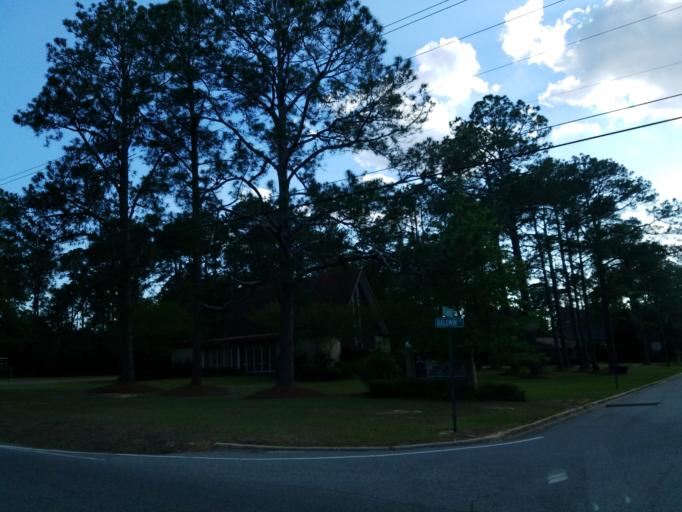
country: US
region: Georgia
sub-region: Tift County
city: Tifton
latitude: 31.4665
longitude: -83.5193
